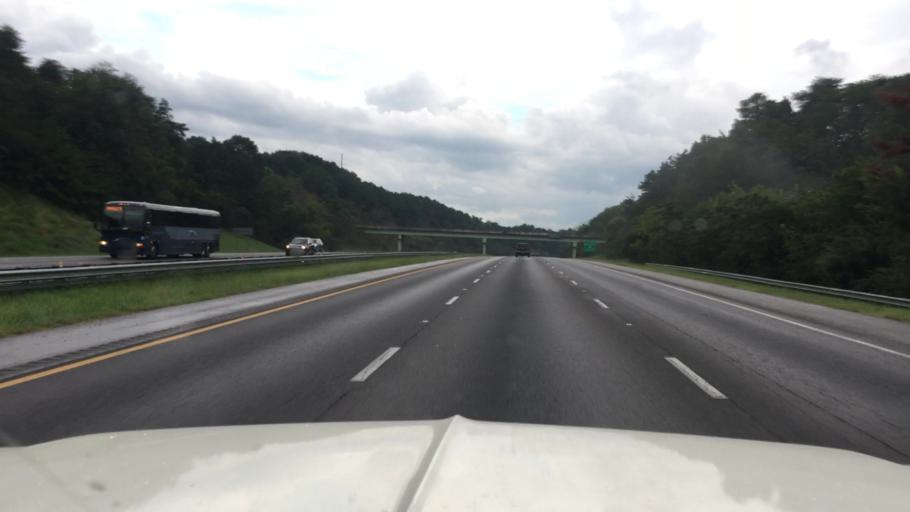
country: US
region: Alabama
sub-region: Jefferson County
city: Mount Olive
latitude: 33.6871
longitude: -86.8300
